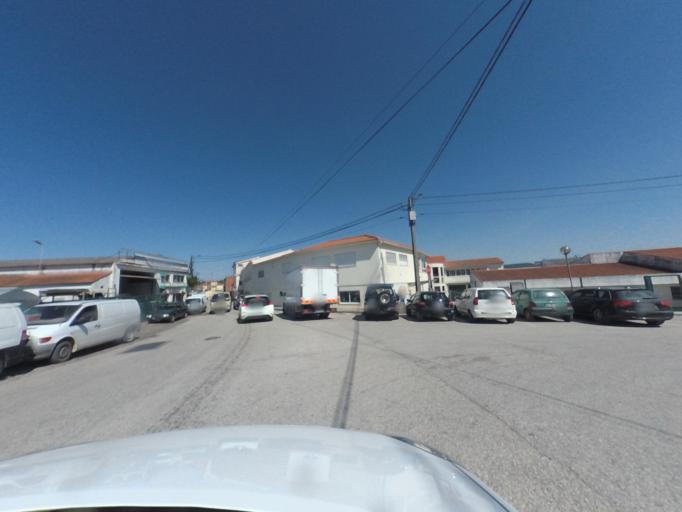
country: PT
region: Leiria
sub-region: Alcobaca
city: Turquel
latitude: 39.4668
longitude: -8.9781
